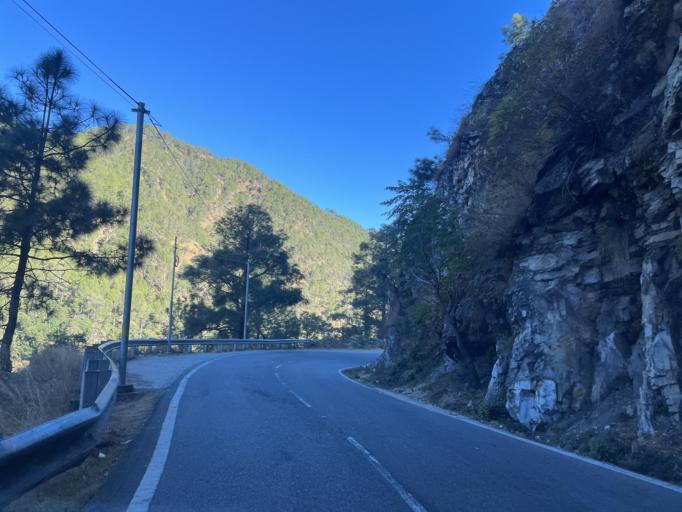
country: IN
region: Uttarakhand
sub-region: Naini Tal
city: Bhowali
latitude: 29.4046
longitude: 79.5104
